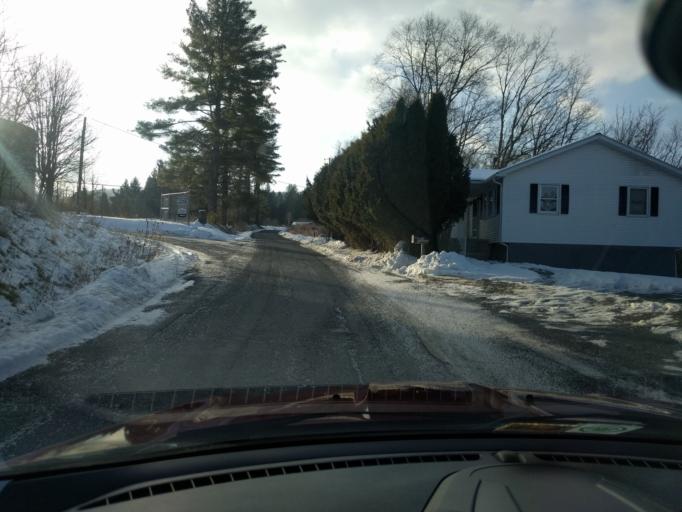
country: US
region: West Virginia
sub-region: Pocahontas County
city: Marlinton
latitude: 38.2174
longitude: -80.0813
